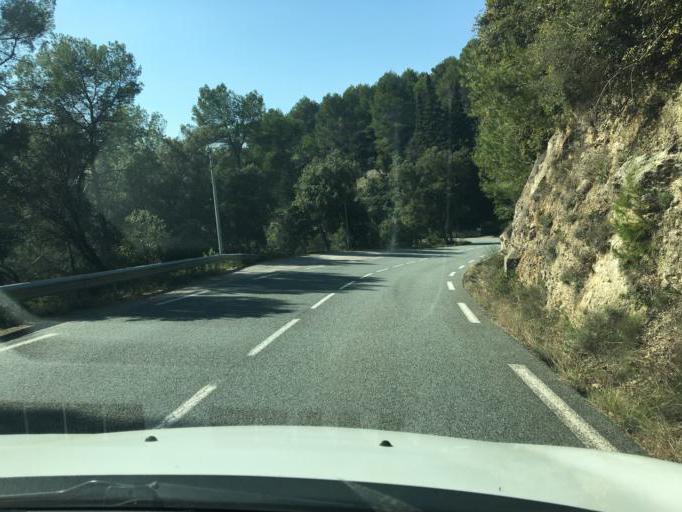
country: FR
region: Provence-Alpes-Cote d'Azur
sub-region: Departement du Var
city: Callas
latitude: 43.5992
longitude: 6.5478
